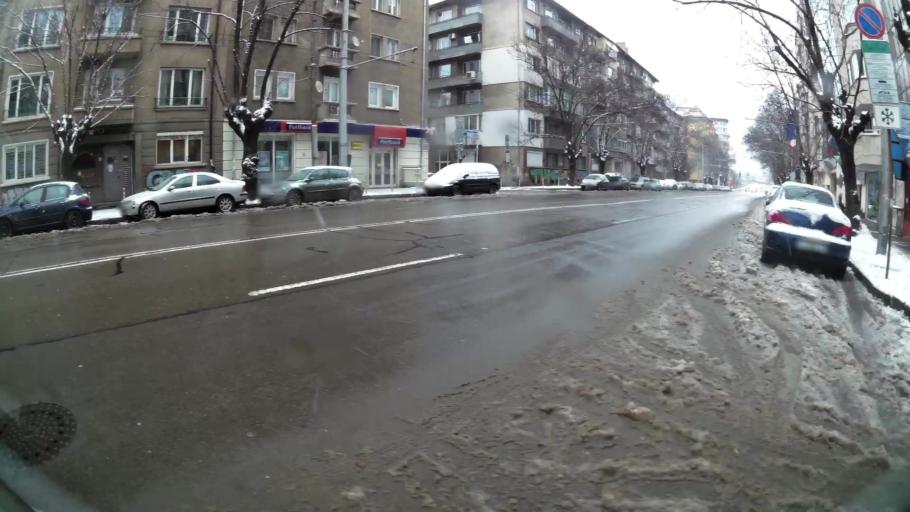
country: BG
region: Sofia-Capital
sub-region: Stolichna Obshtina
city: Sofia
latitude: 42.6993
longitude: 23.3402
